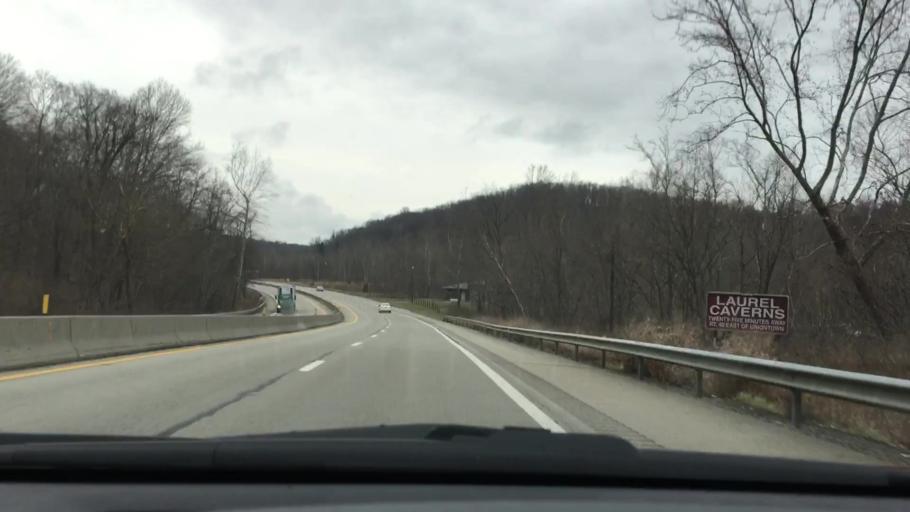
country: US
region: Pennsylvania
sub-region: Fayette County
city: Oliver
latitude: 39.9906
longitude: -79.7655
